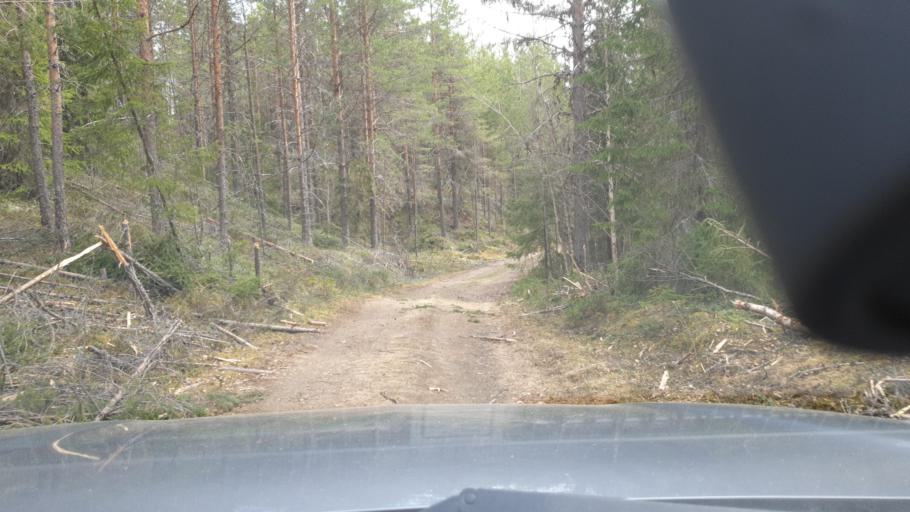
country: SE
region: Vaesternorrland
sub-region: Ange Kommun
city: Ange
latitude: 62.1869
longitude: 15.6166
